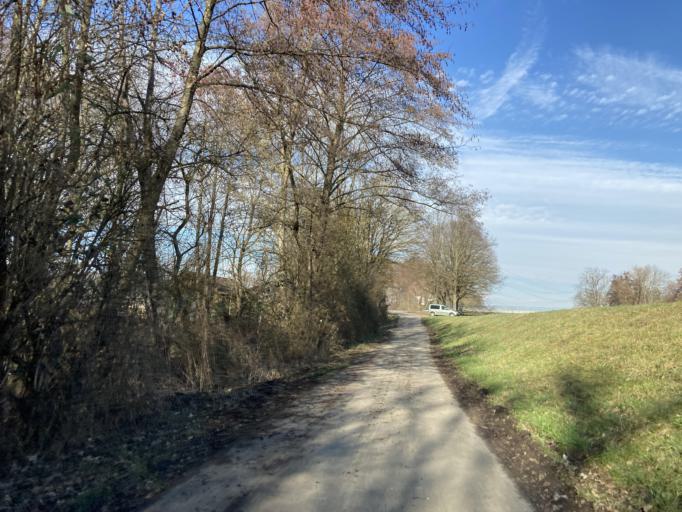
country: DE
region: Baden-Wuerttemberg
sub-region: Freiburg Region
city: Eichstetten
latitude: 48.0687
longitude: 7.7573
